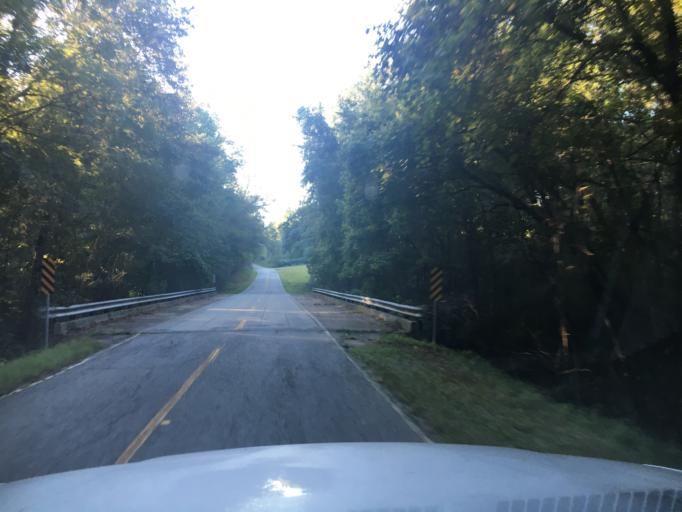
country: US
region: South Carolina
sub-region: Spartanburg County
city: Woodruff
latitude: 34.7690
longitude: -81.9647
